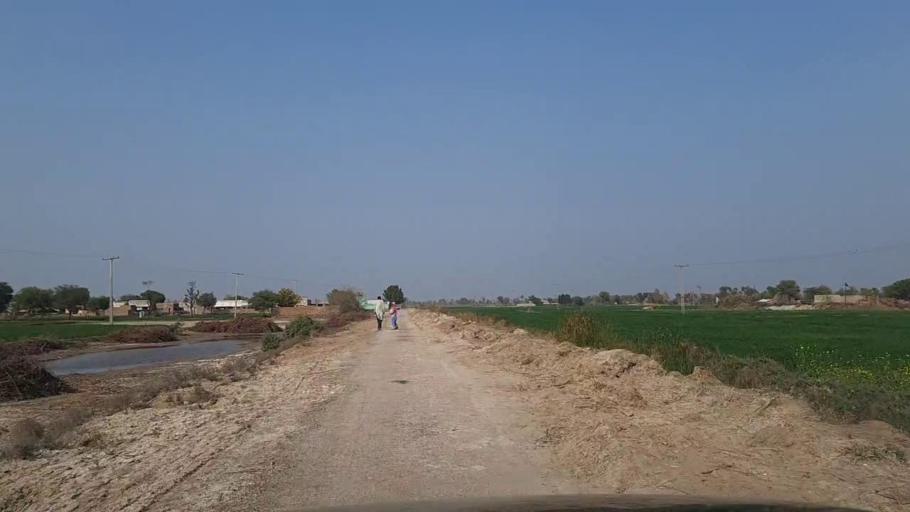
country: PK
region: Sindh
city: Daur
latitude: 26.4086
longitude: 68.4188
